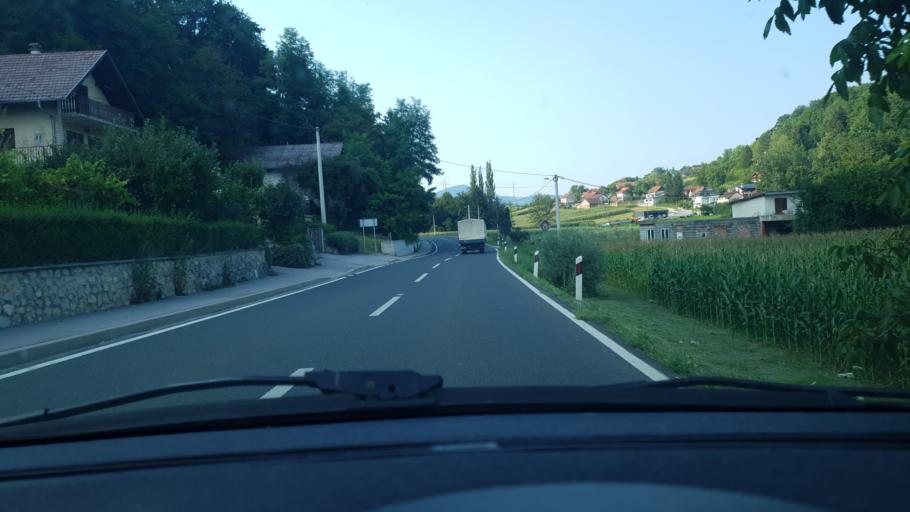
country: HR
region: Krapinsko-Zagorska
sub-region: Grad Krapina
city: Krapina
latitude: 46.1069
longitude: 15.9060
